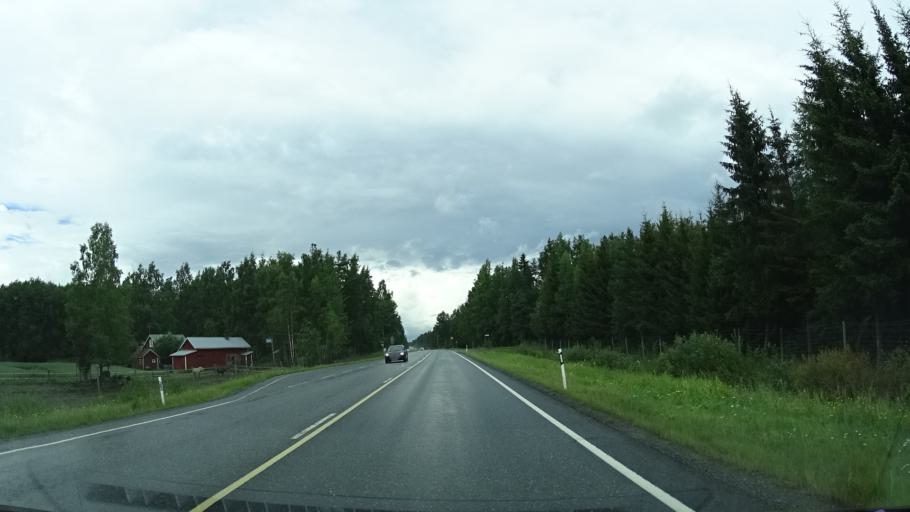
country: FI
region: Haeme
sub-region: Haemeenlinna
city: Kalvola
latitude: 61.1460
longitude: 24.0611
